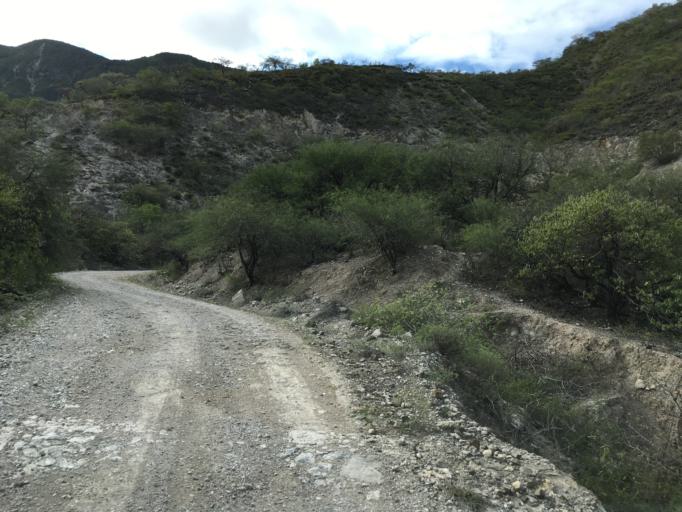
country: MX
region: Hidalgo
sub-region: Metztitlan
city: Fontezuelas
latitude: 20.6383
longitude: -98.9325
